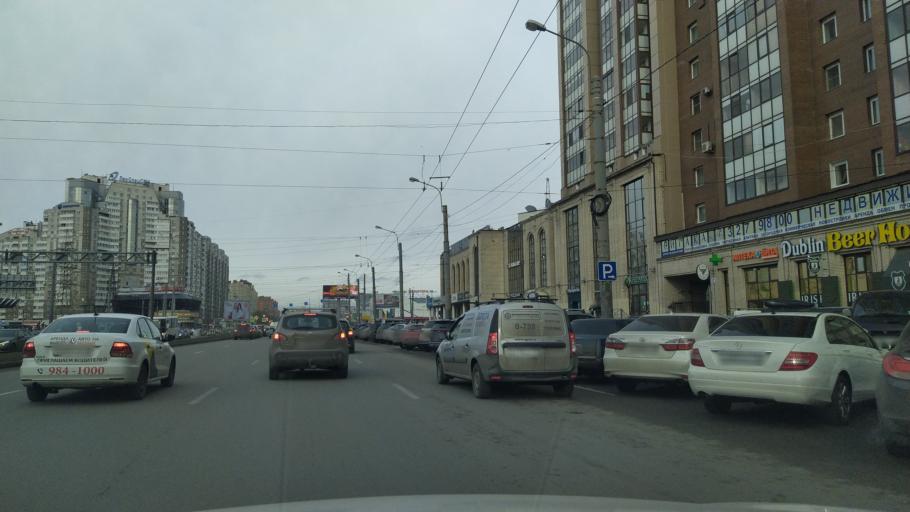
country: RU
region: Leningrad
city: Chernaya Rechka
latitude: 60.0011
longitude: 30.2988
